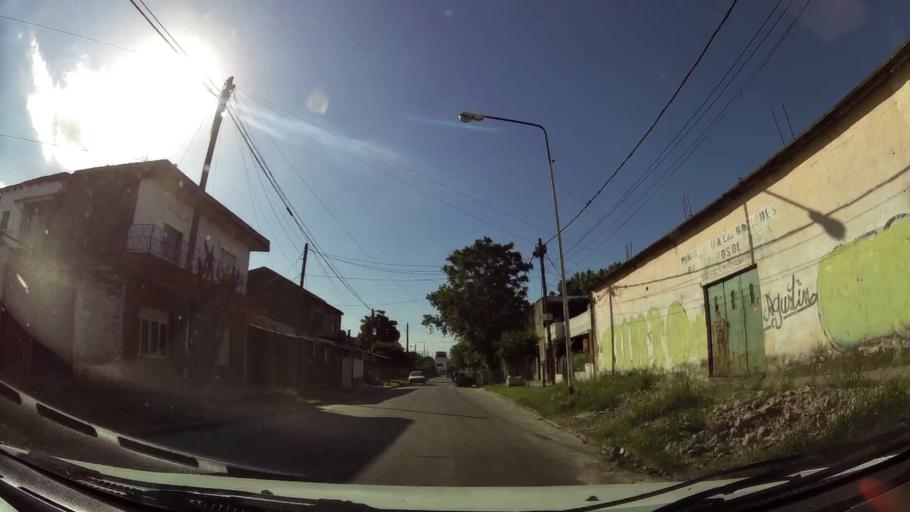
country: AR
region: Buenos Aires
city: Hurlingham
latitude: -34.5620
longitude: -58.6237
